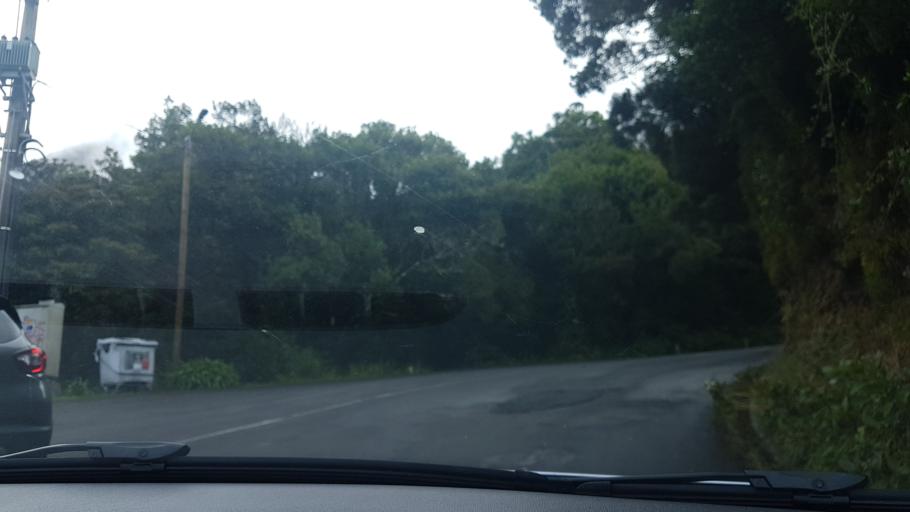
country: PT
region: Madeira
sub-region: Sao Vicente
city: Sao Vicente
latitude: 32.7616
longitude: -17.0160
